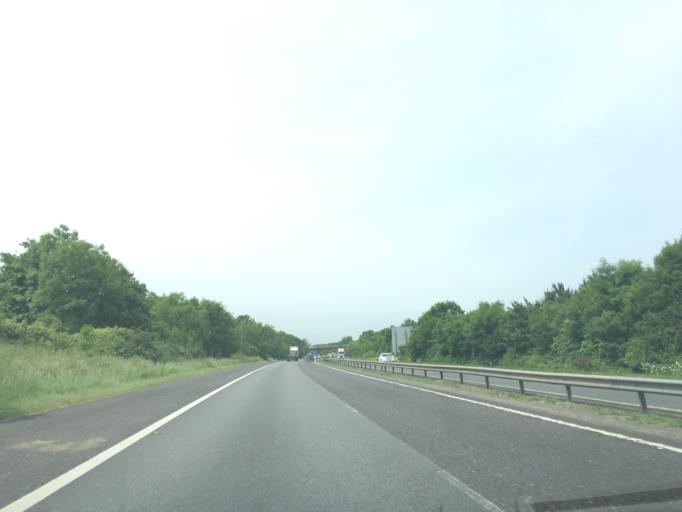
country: GB
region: England
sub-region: Kent
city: Borough Green
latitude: 51.3010
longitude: 0.3149
